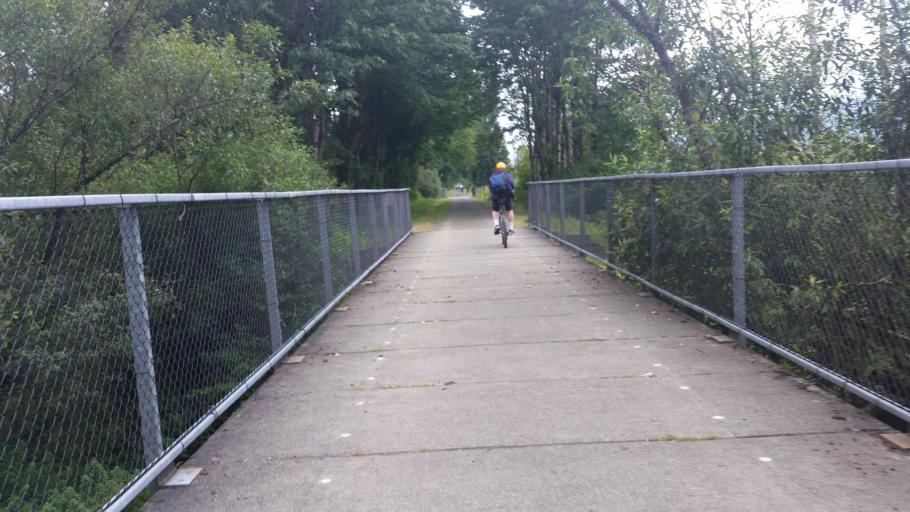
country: US
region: Washington
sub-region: King County
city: Snoqualmie
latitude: 47.5245
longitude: -121.8029
